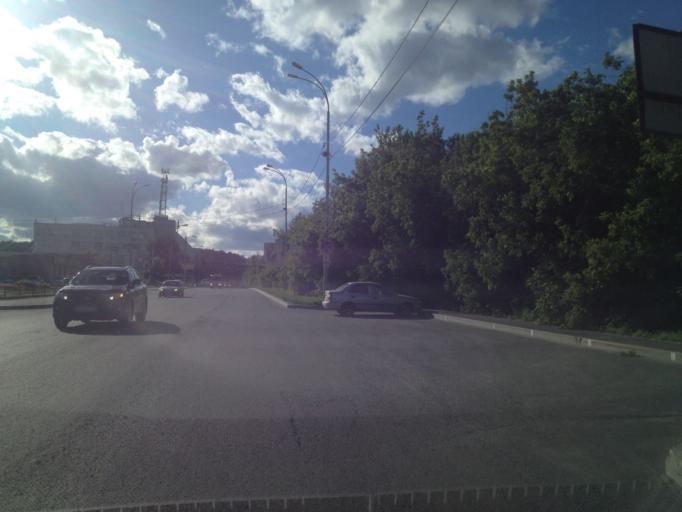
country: RU
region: Sverdlovsk
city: Sovkhoznyy
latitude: 56.8123
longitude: 60.5405
